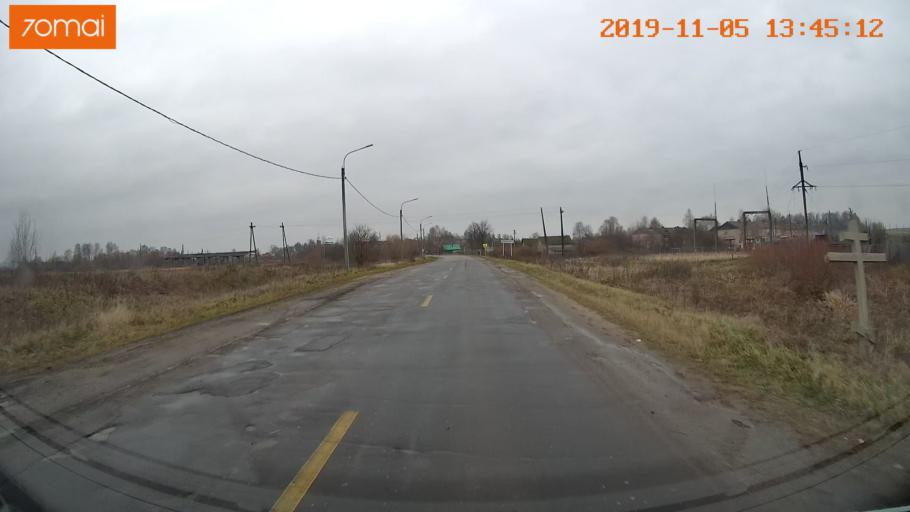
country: RU
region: Ivanovo
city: Shuya
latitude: 56.9868
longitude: 41.4122
